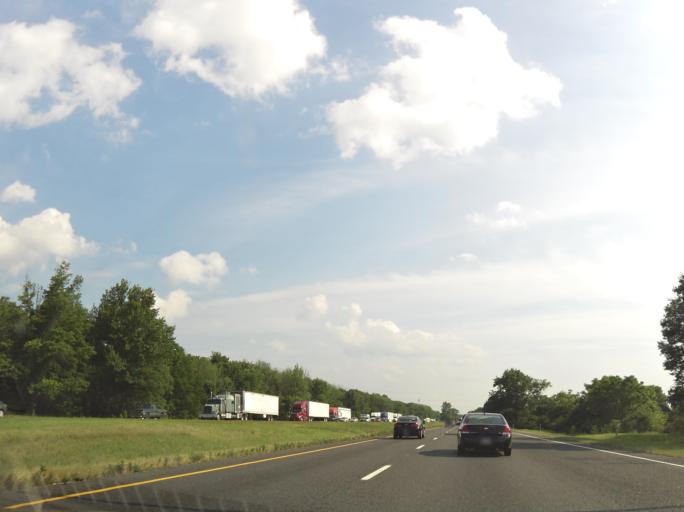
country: US
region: Maryland
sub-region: Washington County
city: Maugansville
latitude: 39.6847
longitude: -77.7334
